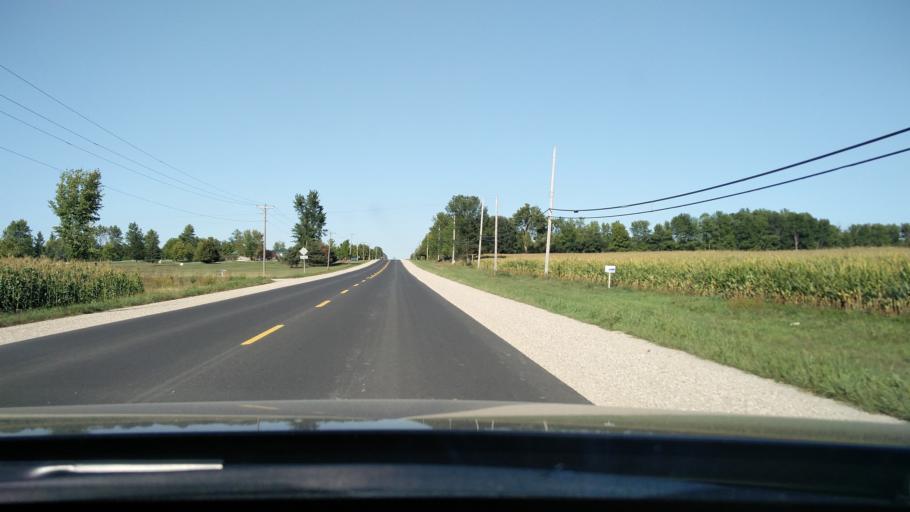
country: CA
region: Ontario
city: Perth
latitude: 44.8589
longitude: -76.2931
